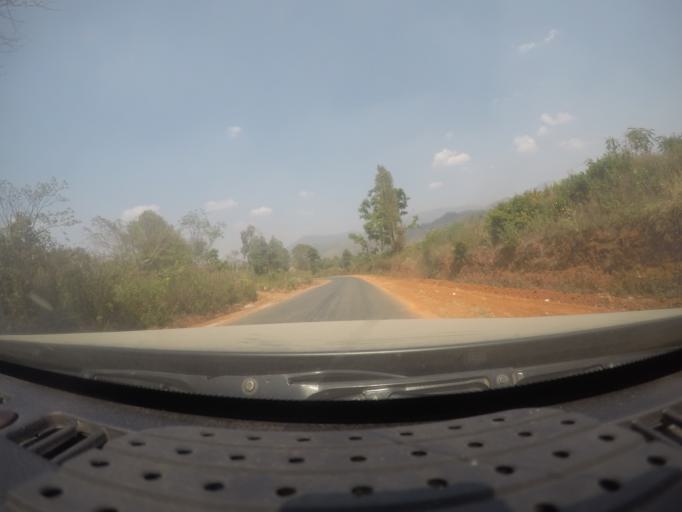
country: MM
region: Shan
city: Taunggyi
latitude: 21.0661
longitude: 96.5129
